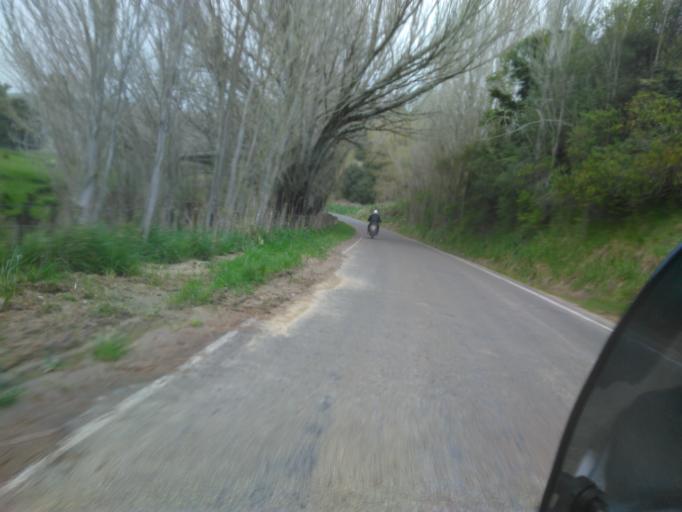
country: NZ
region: Gisborne
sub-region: Gisborne District
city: Gisborne
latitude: -38.6422
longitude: 177.7038
